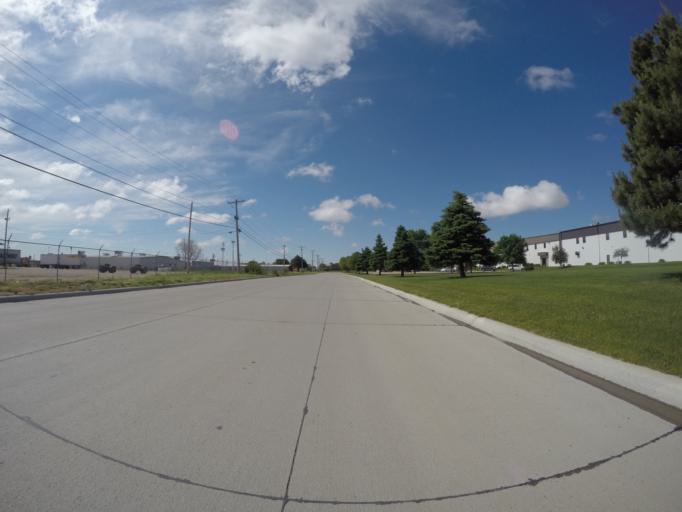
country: US
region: Nebraska
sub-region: Buffalo County
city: Kearney
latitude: 40.6802
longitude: -99.0876
